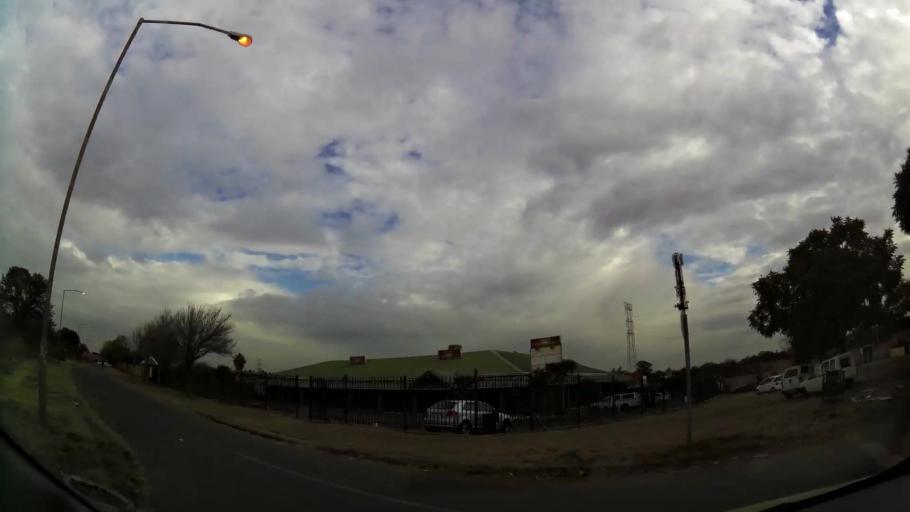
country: ZA
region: Gauteng
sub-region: City of Tshwane Metropolitan Municipality
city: Pretoria
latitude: -25.7020
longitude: 28.3009
